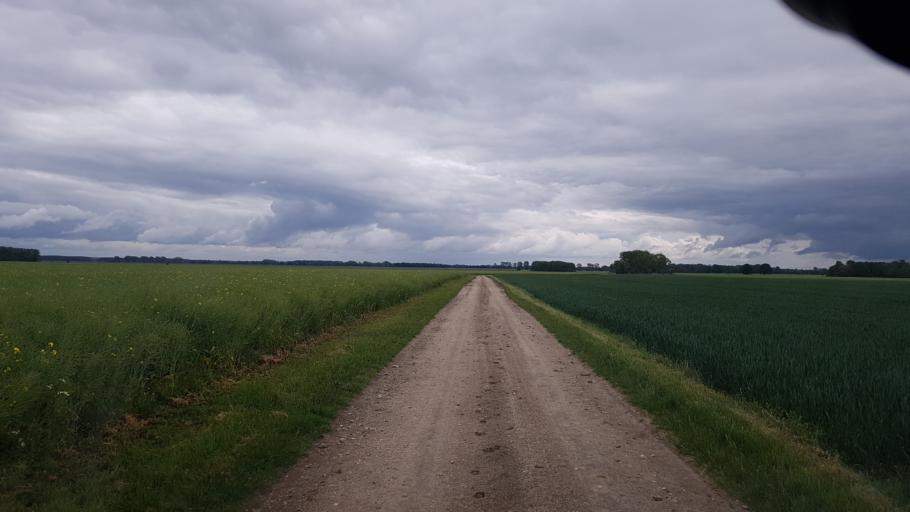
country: DE
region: Brandenburg
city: Doberlug-Kirchhain
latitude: 51.6749
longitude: 13.5241
